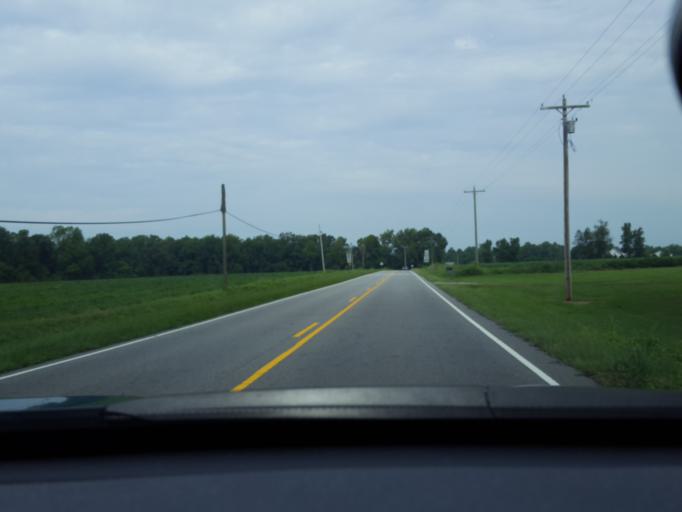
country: US
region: North Carolina
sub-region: Chowan County
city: Edenton
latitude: 36.1646
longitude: -76.6570
